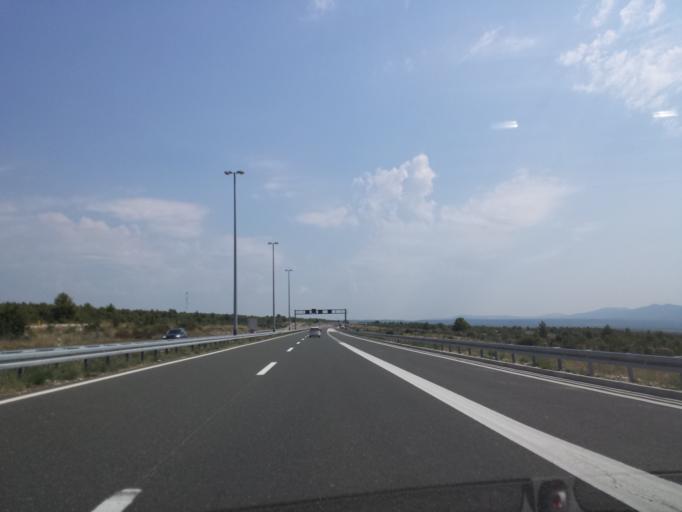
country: HR
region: Sibensko-Kniniska
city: Zaton
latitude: 43.8555
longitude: 15.8484
